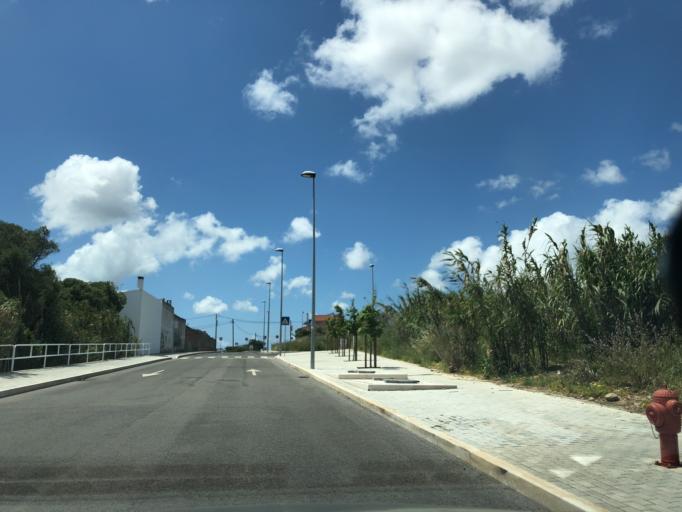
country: PT
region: Lisbon
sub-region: Cascais
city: Sao Domingos de Rana
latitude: 38.7044
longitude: -9.3274
